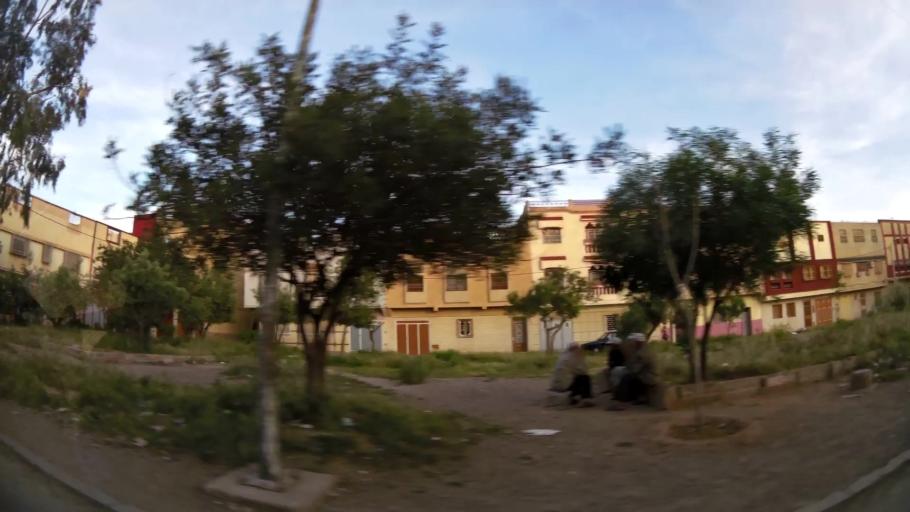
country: MA
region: Oriental
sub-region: Oujda-Angad
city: Oujda
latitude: 34.6789
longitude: -1.8803
